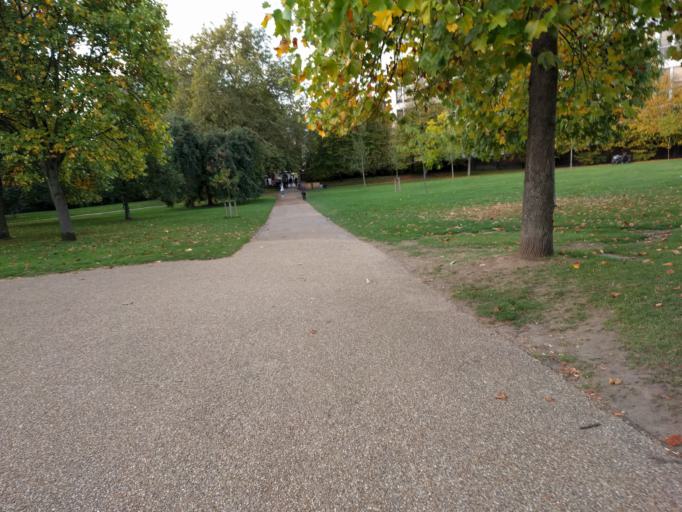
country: GB
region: England
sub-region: Greater London
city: Kensington
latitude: 51.5033
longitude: -0.1868
